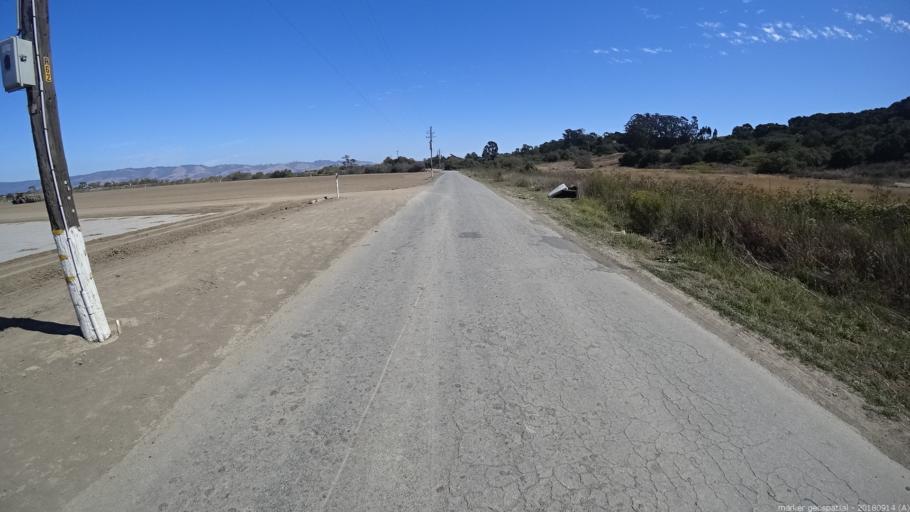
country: US
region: California
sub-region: Monterey County
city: Pajaro
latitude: 36.8757
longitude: -121.7757
